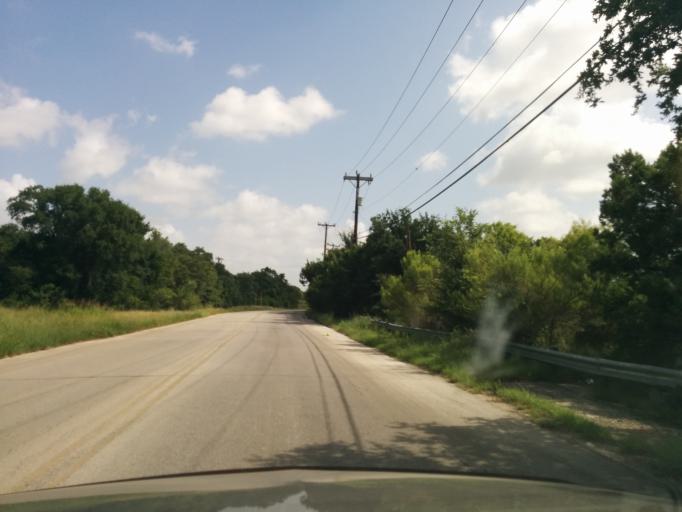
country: US
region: Texas
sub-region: Bexar County
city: Cross Mountain
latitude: 29.6003
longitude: -98.6292
